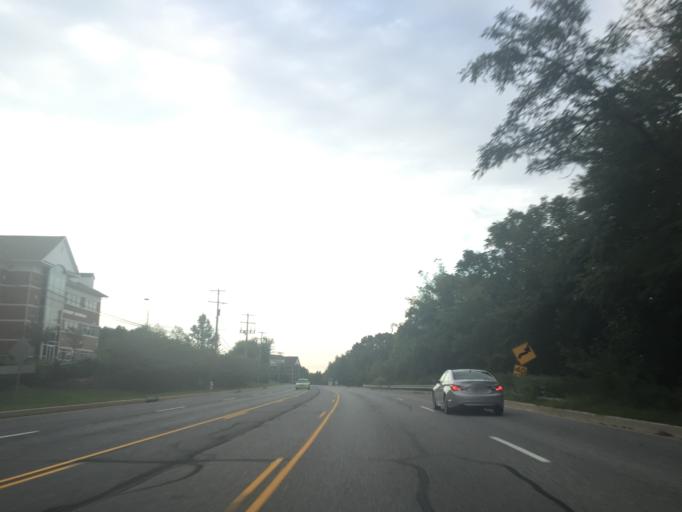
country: US
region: Maryland
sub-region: Anne Arundel County
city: South Gate
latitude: 39.0887
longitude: -76.6234
